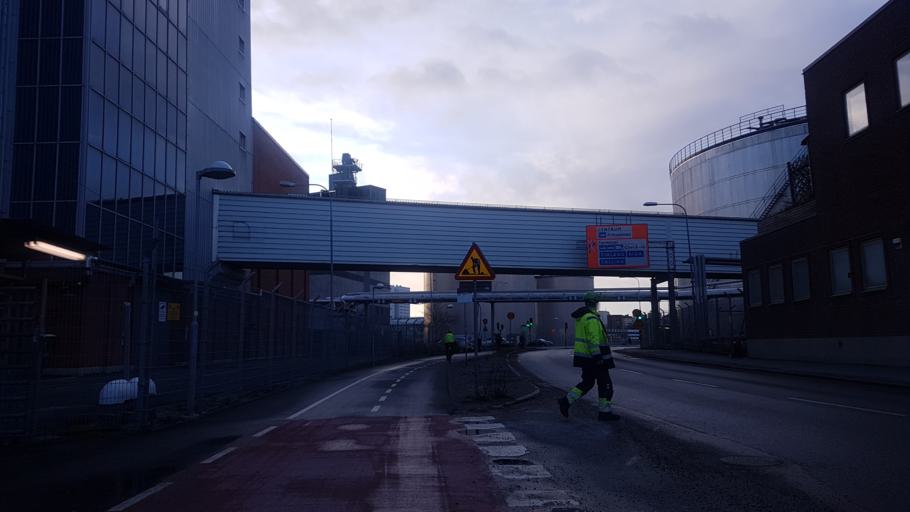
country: SE
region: Stockholm
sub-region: Stockholms Kommun
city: OEstermalm
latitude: 59.3541
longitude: 18.1082
